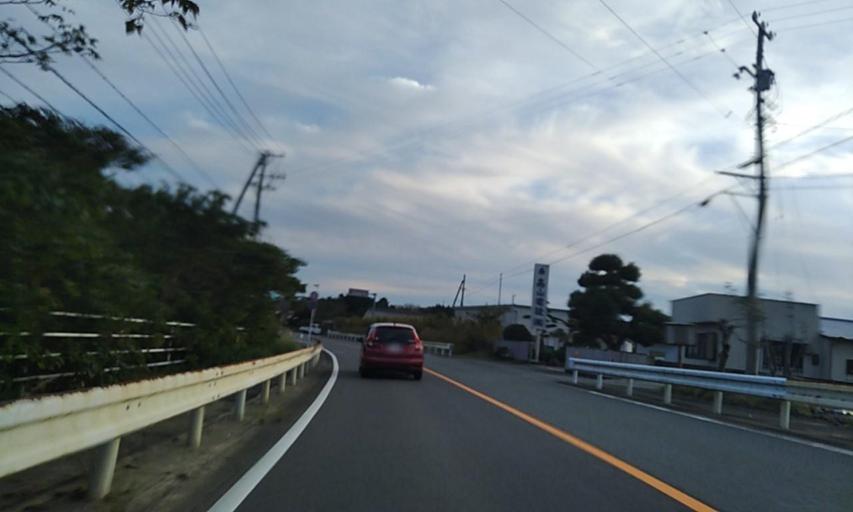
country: JP
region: Mie
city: Toba
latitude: 34.2981
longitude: 136.8753
